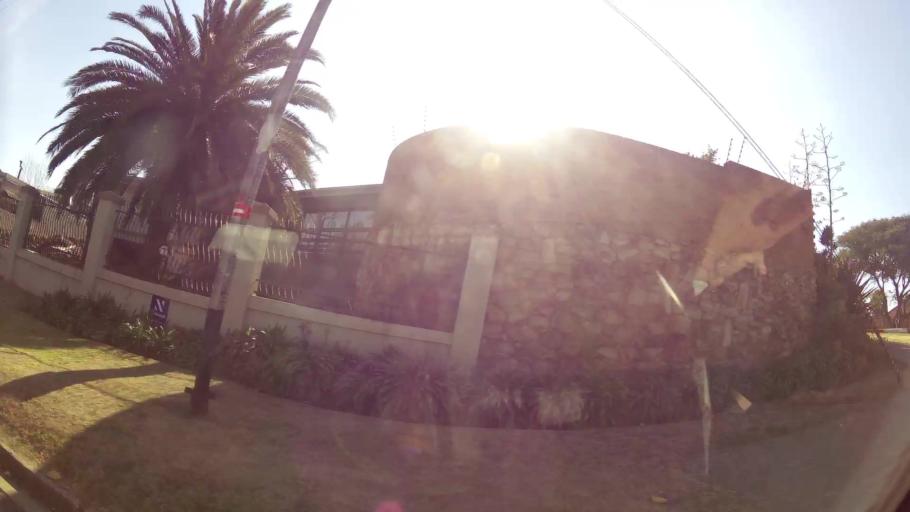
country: ZA
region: Gauteng
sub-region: City of Johannesburg Metropolitan Municipality
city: Johannesburg
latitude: -26.2633
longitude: 28.0702
